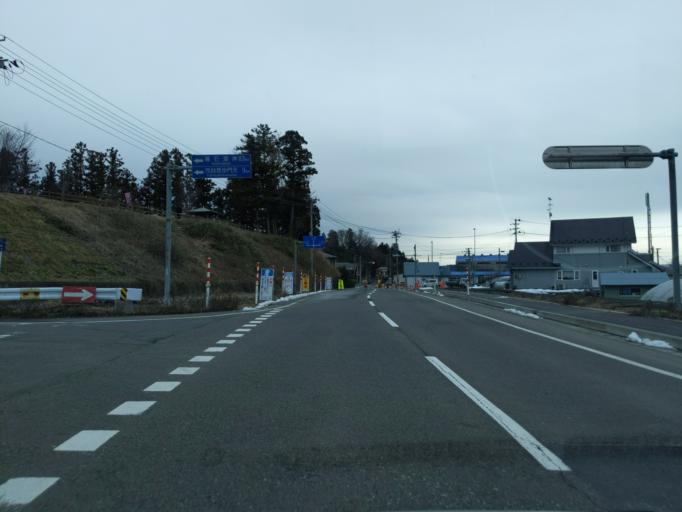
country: JP
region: Iwate
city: Mizusawa
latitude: 39.1801
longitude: 141.1904
